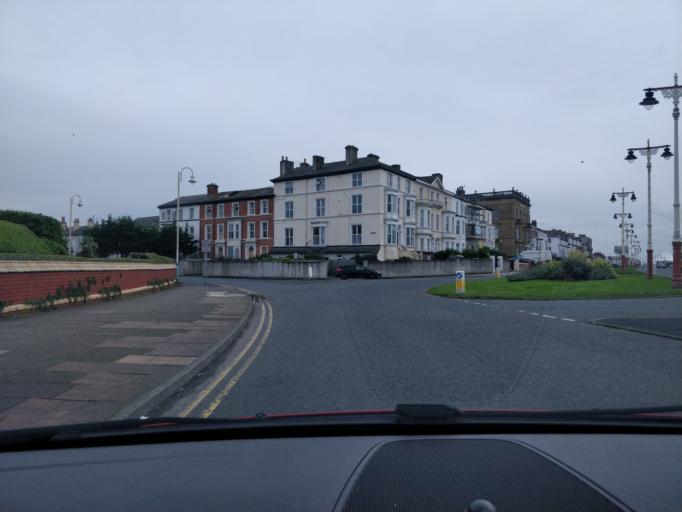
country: GB
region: England
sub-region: Sefton
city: Southport
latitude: 53.6536
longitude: -3.0038
